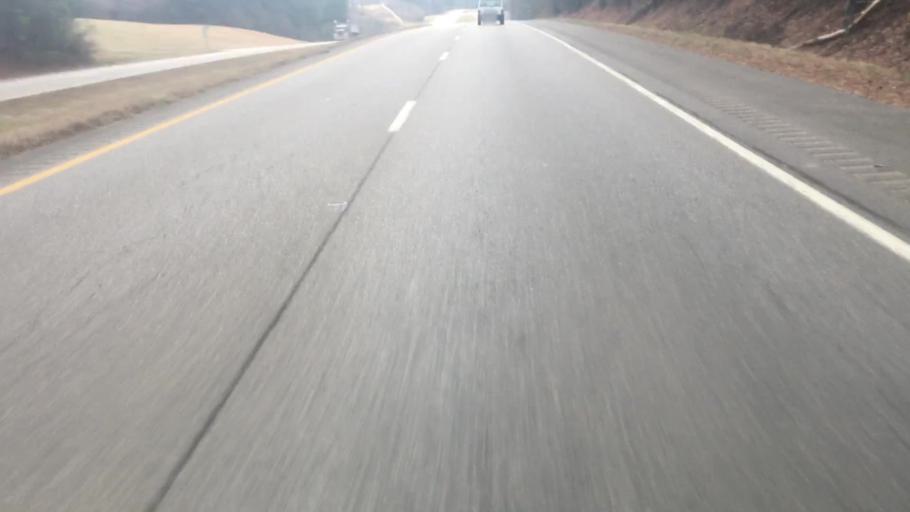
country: US
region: Alabama
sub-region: Walker County
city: Sumiton
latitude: 33.7189
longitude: -86.9997
